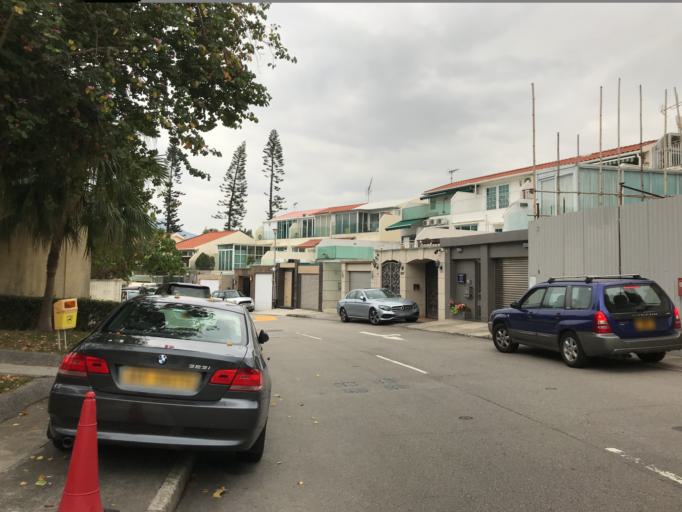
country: HK
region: Tai Po
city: Tai Po
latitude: 22.4652
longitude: 114.1553
